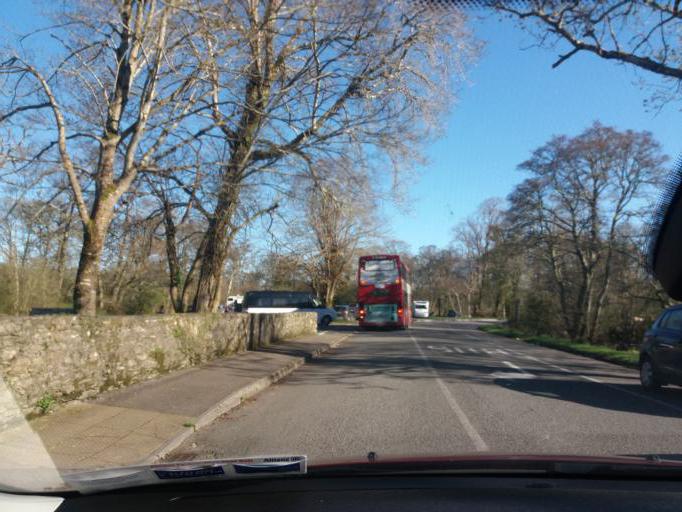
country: IE
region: Munster
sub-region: Ciarrai
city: Cill Airne
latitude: 52.0422
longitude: -9.5299
